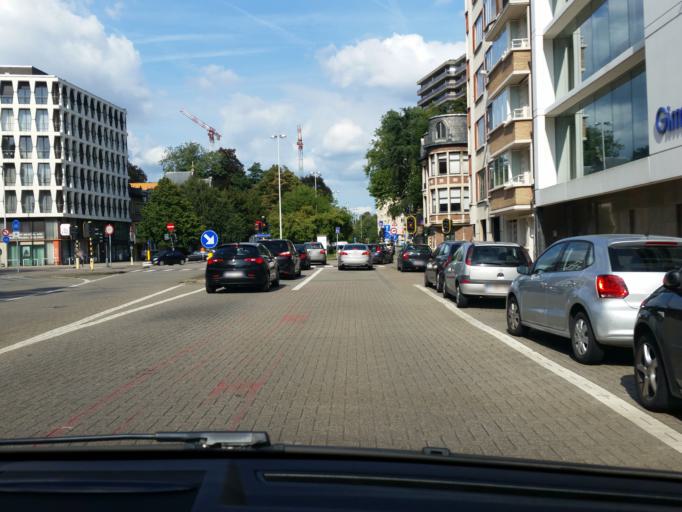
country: BE
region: Flanders
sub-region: Provincie Antwerpen
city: Antwerpen
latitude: 51.1950
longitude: 4.4091
